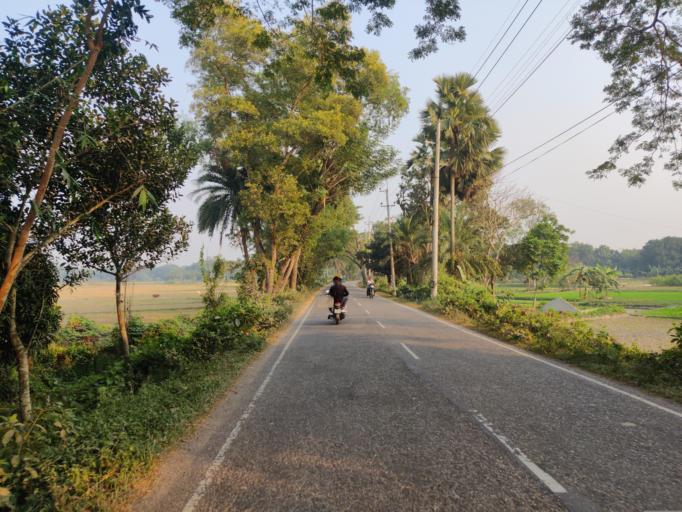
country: BD
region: Dhaka
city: Narsingdi
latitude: 24.0945
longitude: 90.7210
